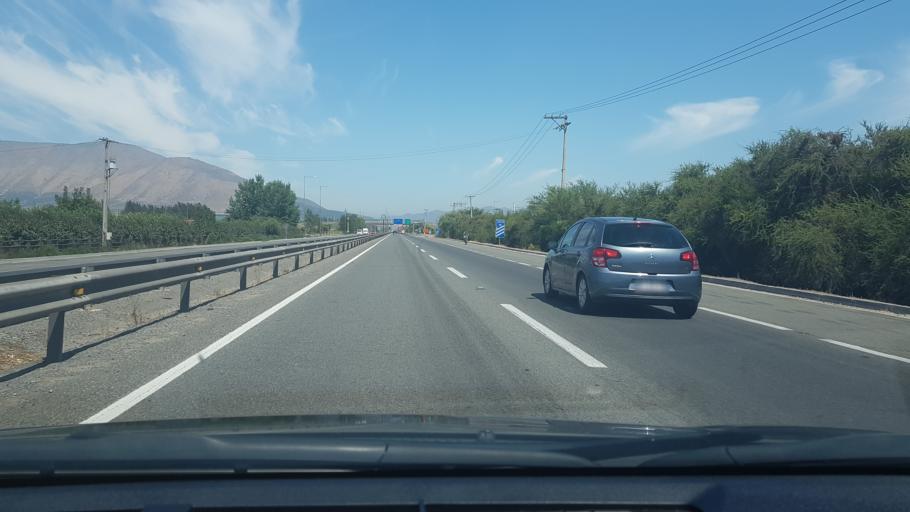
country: CL
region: Valparaiso
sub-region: Provincia de San Felipe
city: Llaillay
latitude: -32.8518
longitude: -70.9373
